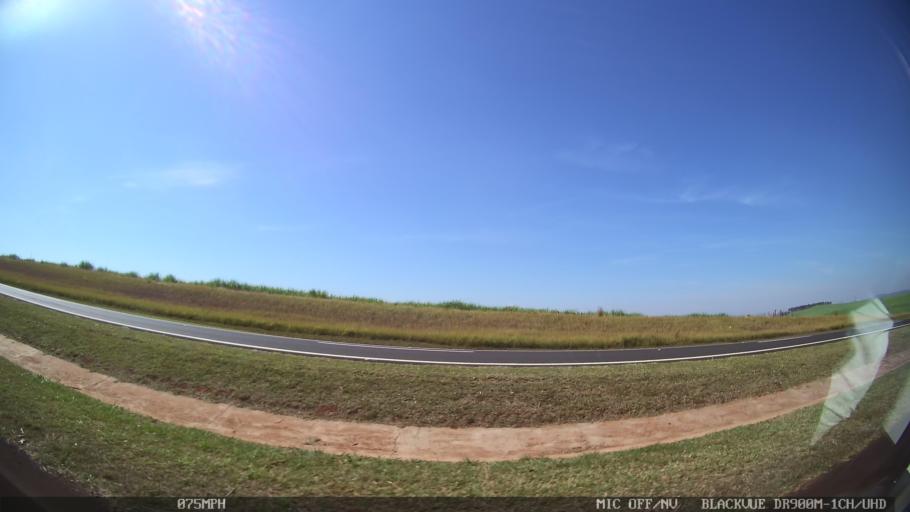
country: BR
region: Sao Paulo
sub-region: Ribeirao Preto
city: Ribeirao Preto
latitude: -21.1747
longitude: -47.8959
